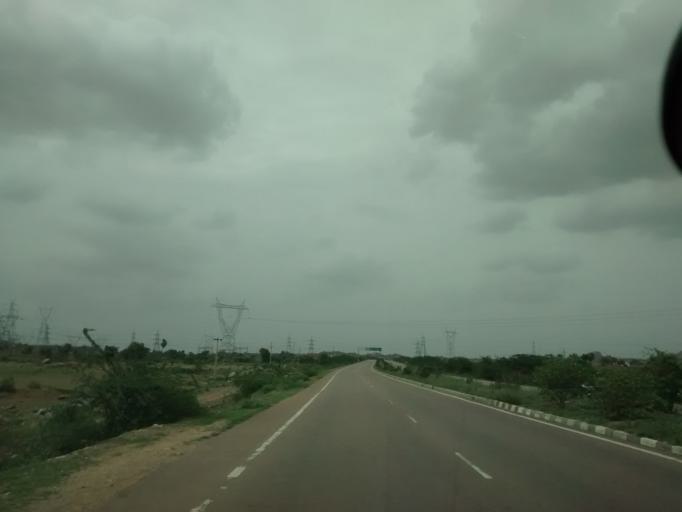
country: IN
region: Andhra Pradesh
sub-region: Kurnool
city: Ramapuram
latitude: 15.1400
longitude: 77.6632
